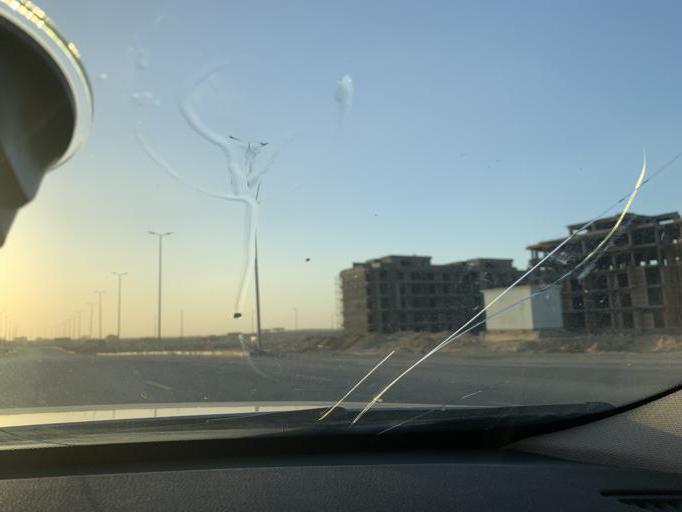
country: EG
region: Muhafazat al Qalyubiyah
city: Al Khankah
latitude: 30.0239
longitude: 31.5899
